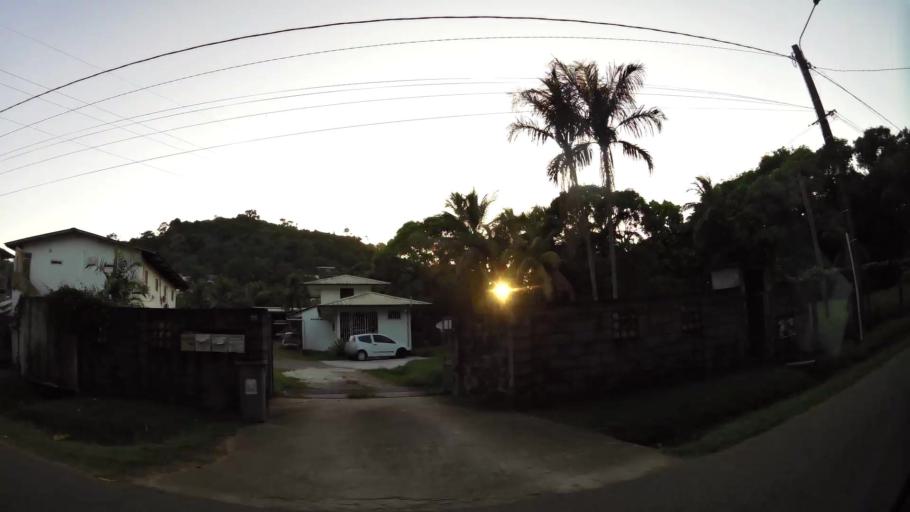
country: GF
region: Guyane
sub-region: Guyane
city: Cayenne
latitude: 4.9233
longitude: -52.3039
